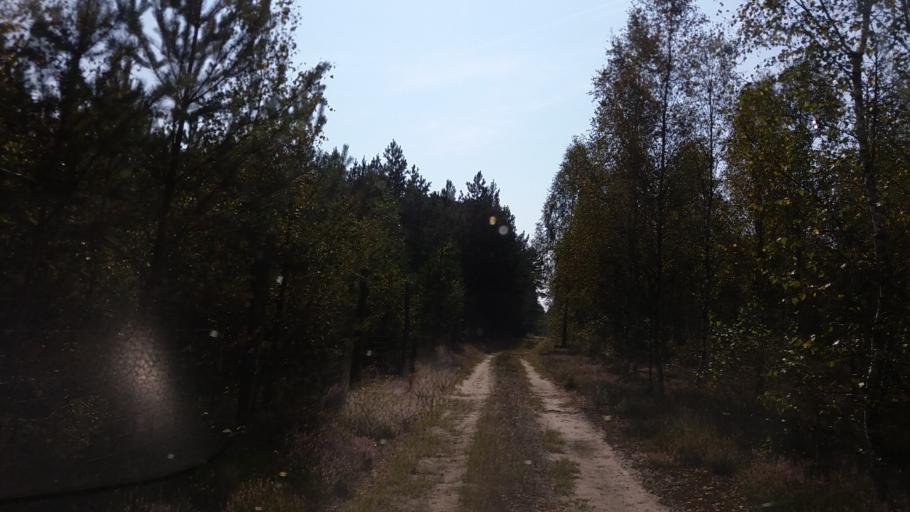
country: PL
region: West Pomeranian Voivodeship
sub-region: Powiat drawski
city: Kalisz Pomorski
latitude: 53.1355
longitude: 15.9420
